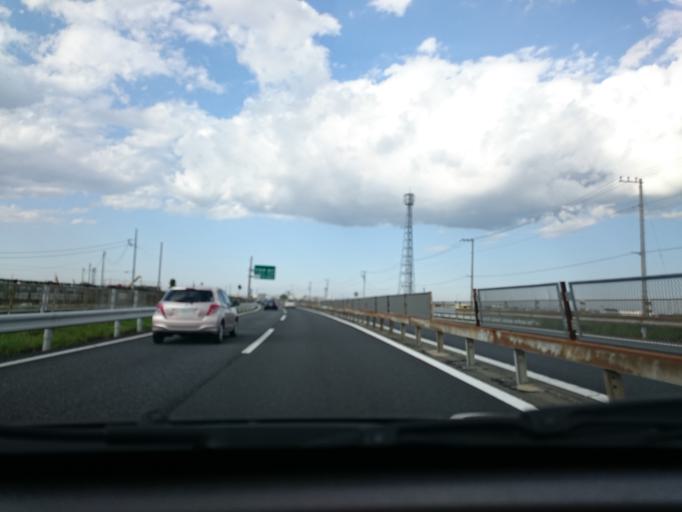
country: JP
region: Kanagawa
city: Isehara
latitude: 35.3784
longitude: 139.3280
